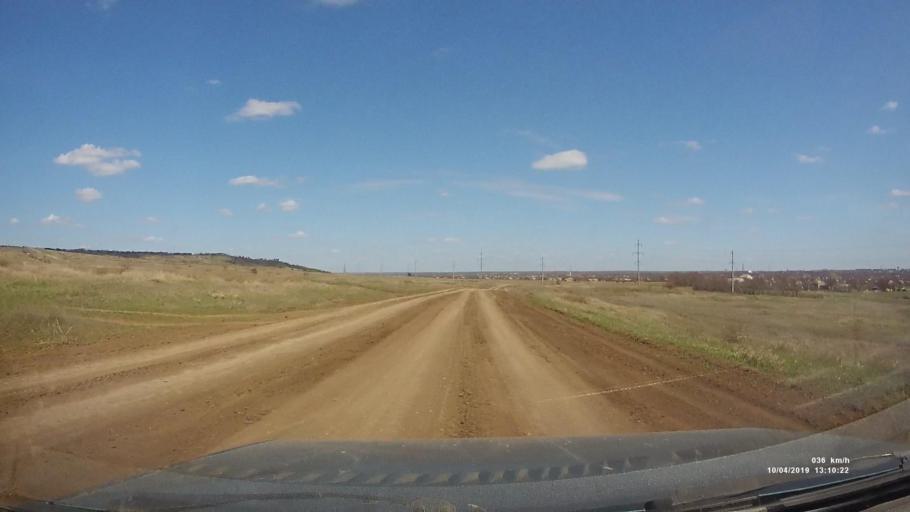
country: RU
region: Rostov
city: Masalovka
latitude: 48.4092
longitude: 40.2472
